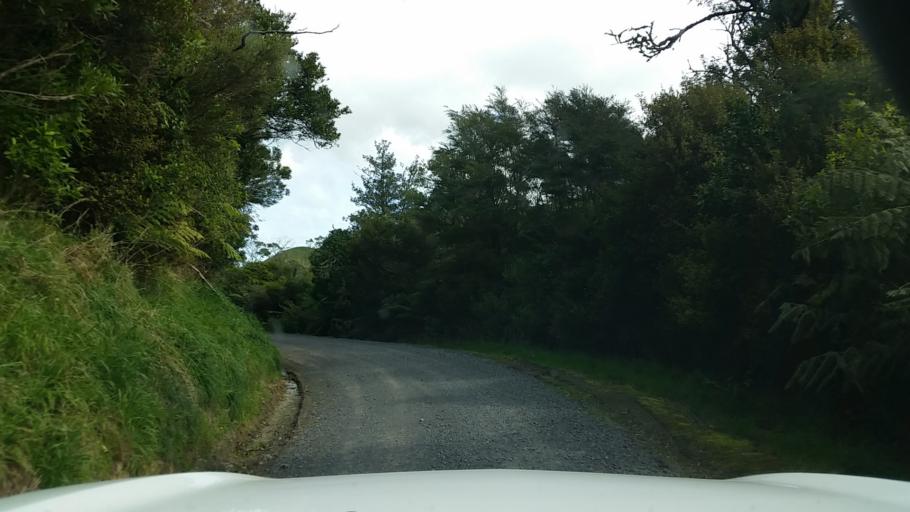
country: NZ
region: Waikato
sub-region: Hauraki District
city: Ngatea
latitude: -37.4795
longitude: 175.4537
